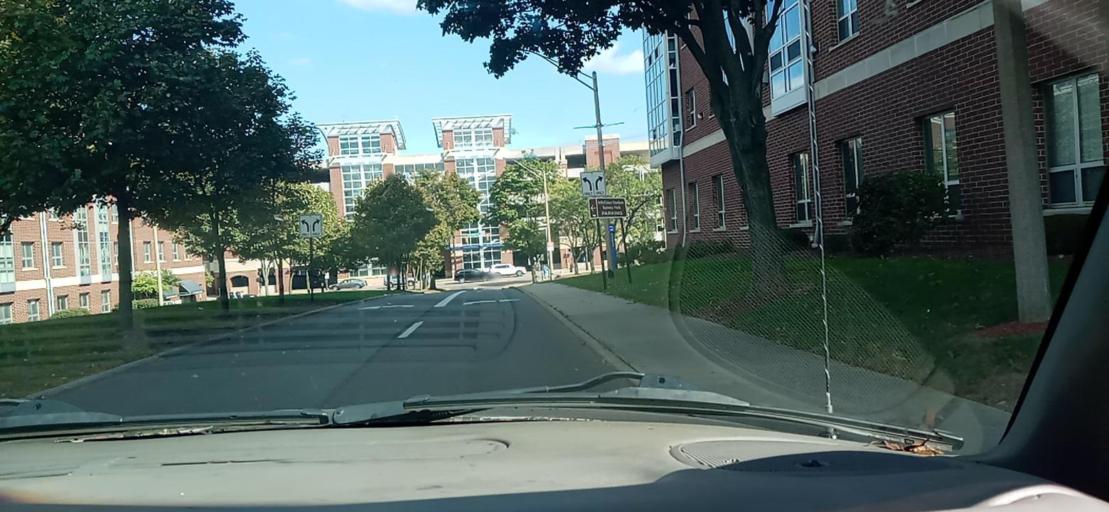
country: US
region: Ohio
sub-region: Summit County
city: Akron
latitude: 41.0730
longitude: -81.5161
